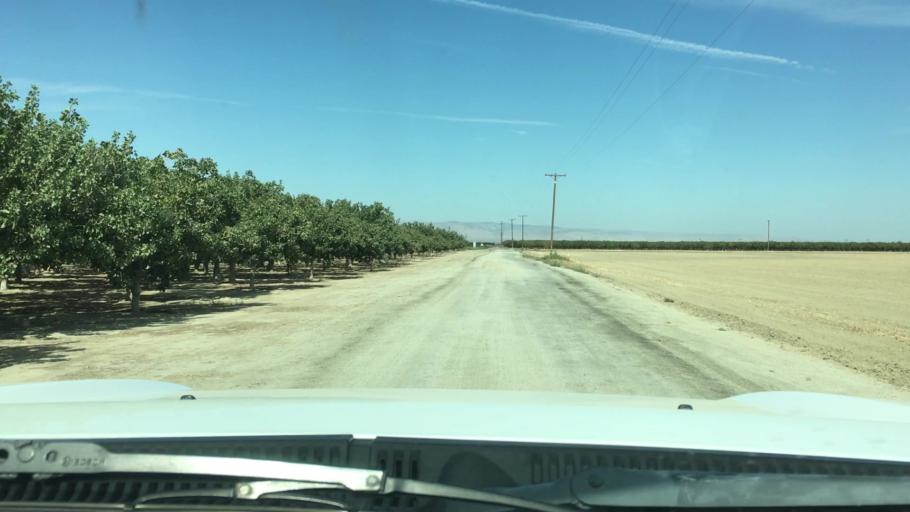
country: US
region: California
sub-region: Kern County
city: Buttonwillow
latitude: 35.3766
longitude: -119.4001
